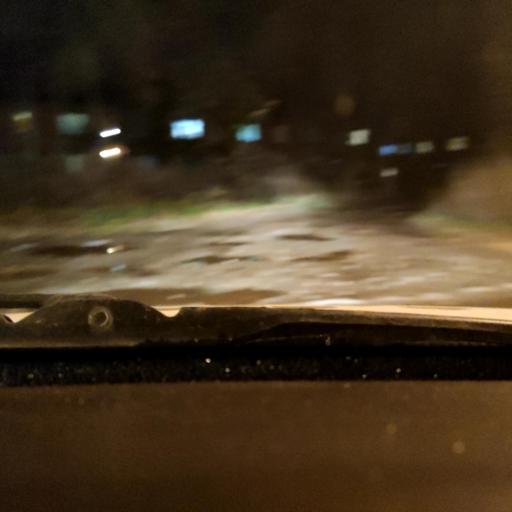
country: RU
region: Perm
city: Perm
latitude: 57.9615
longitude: 56.2323
